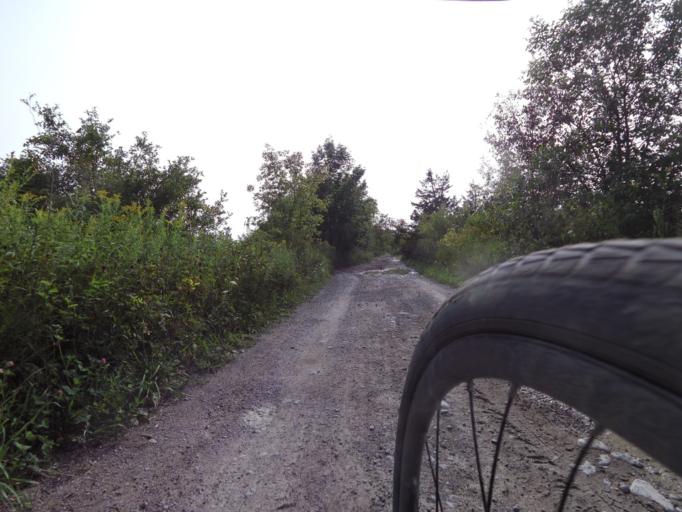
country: CA
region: Ontario
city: Quinte West
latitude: 44.0504
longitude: -77.6152
